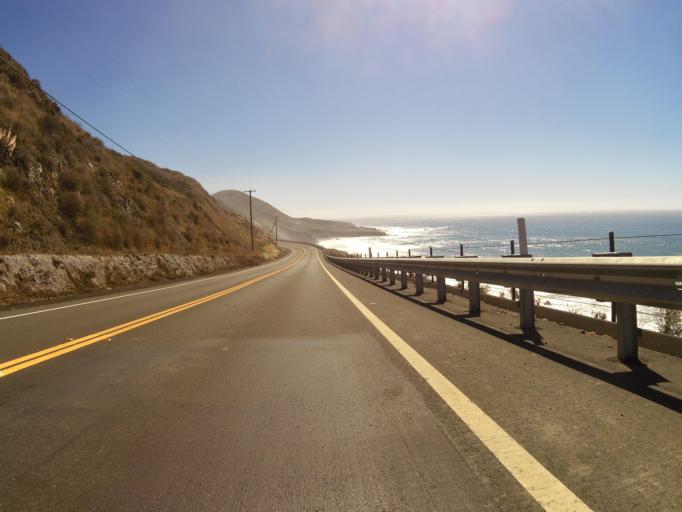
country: US
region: California
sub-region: Mendocino County
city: Fort Bragg
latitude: 39.6198
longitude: -123.7815
